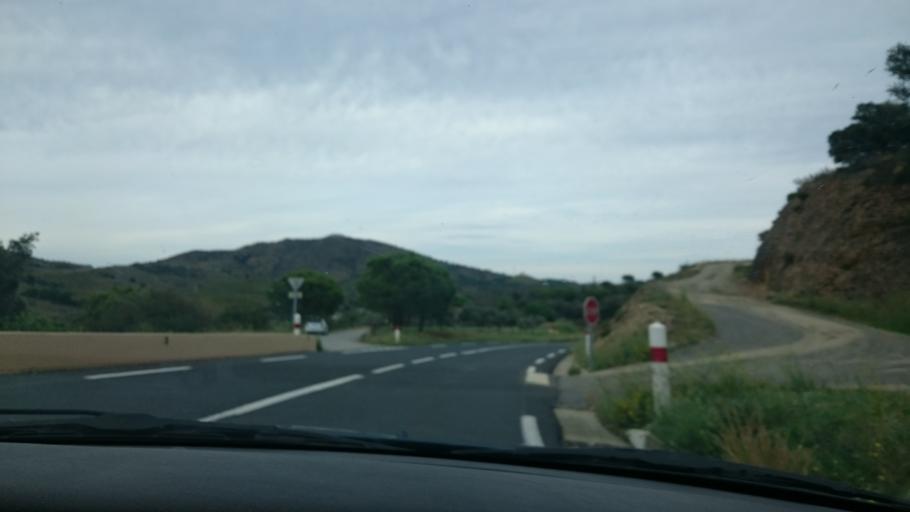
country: FR
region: Languedoc-Roussillon
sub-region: Departement des Pyrenees-Orientales
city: Banyuls de la Marenda
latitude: 42.4958
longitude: 3.1183
